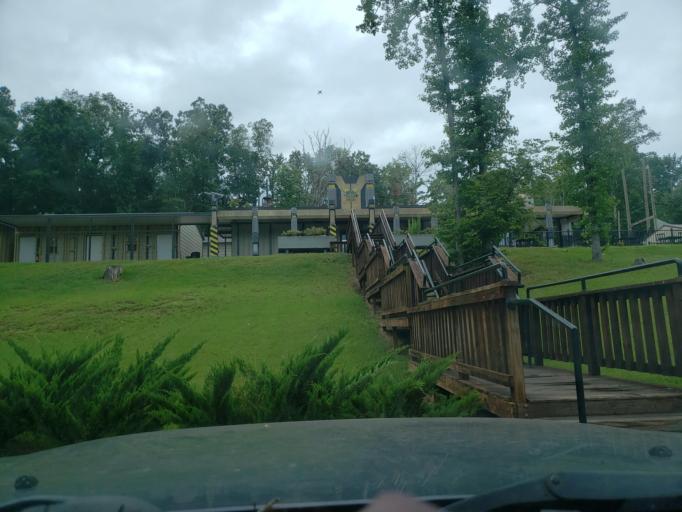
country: US
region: North Carolina
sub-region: Durham County
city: Gorman
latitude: 35.9793
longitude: -78.7360
